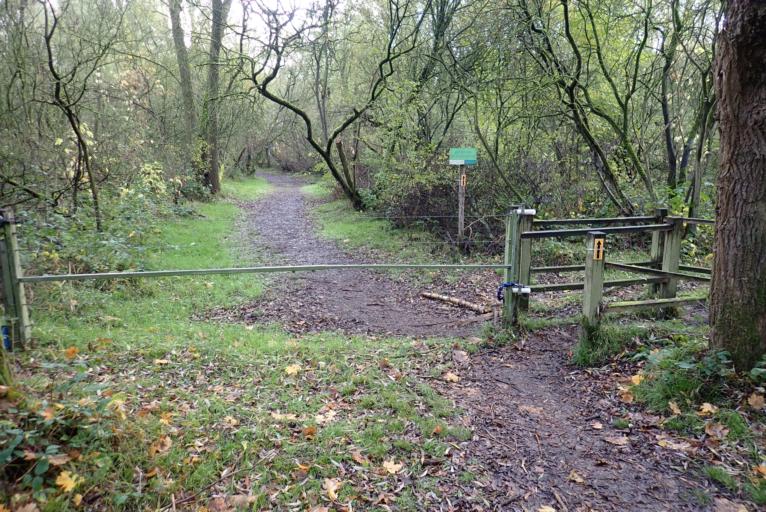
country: BE
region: Flanders
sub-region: Provincie Antwerpen
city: Niel
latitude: 51.1016
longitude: 4.3413
